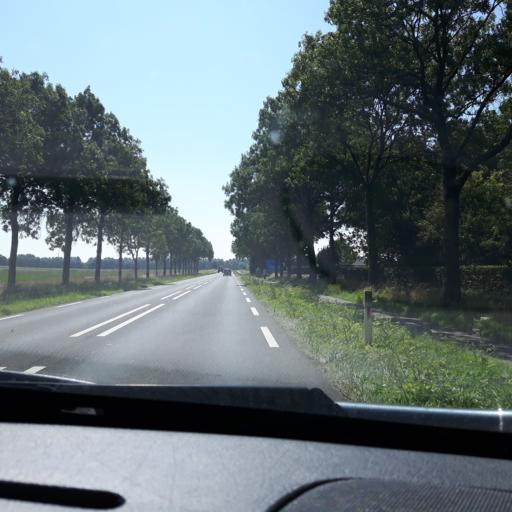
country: NL
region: Zeeland
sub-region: Gemeente Goes
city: Goes
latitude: 51.4699
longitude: 3.9034
